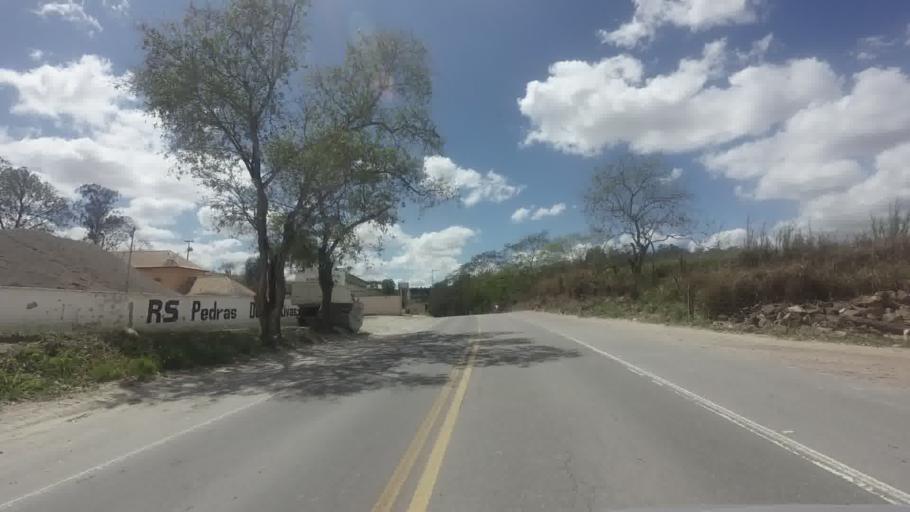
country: BR
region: Minas Gerais
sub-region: Recreio
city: Recreio
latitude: -21.6556
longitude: -42.3612
